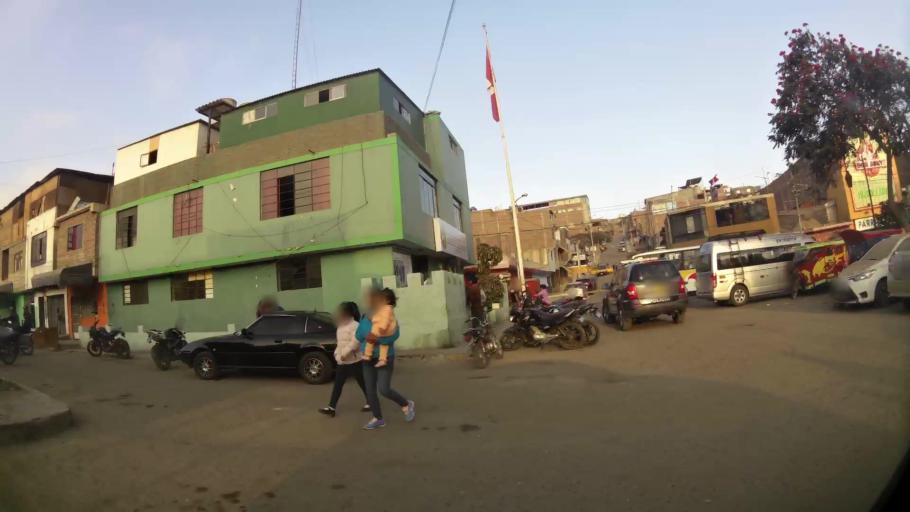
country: PE
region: La Libertad
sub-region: Provincia de Trujillo
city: El Porvenir
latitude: -8.0788
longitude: -78.9995
